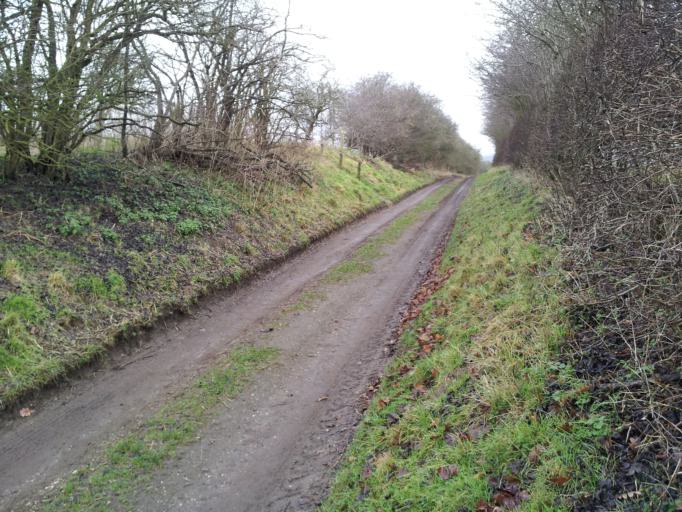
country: GB
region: England
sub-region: East Riding of Yorkshire
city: Ellerker
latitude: 53.7482
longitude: -0.5927
